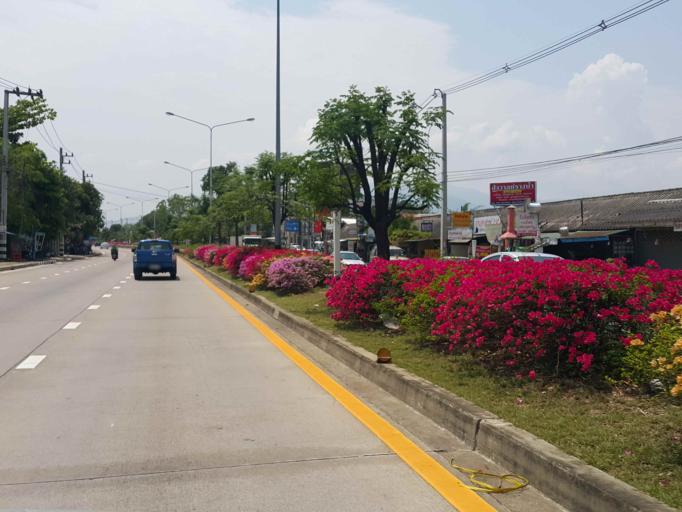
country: TH
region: Chiang Mai
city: Saraphi
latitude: 18.7433
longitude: 98.9972
